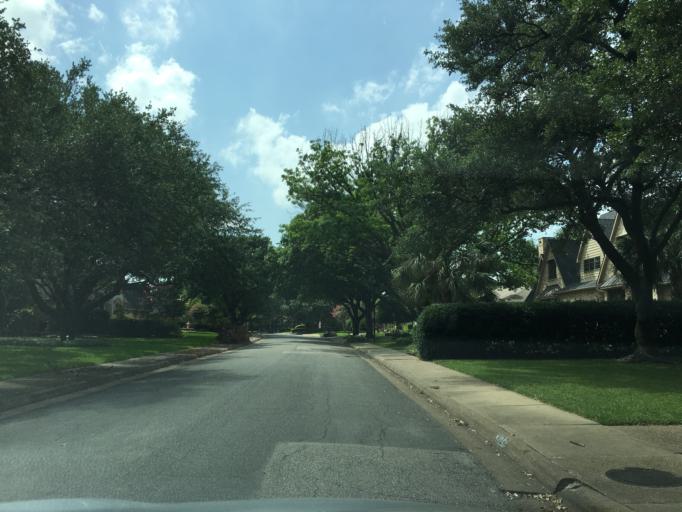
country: US
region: Texas
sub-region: Dallas County
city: University Park
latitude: 32.8767
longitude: -96.7816
